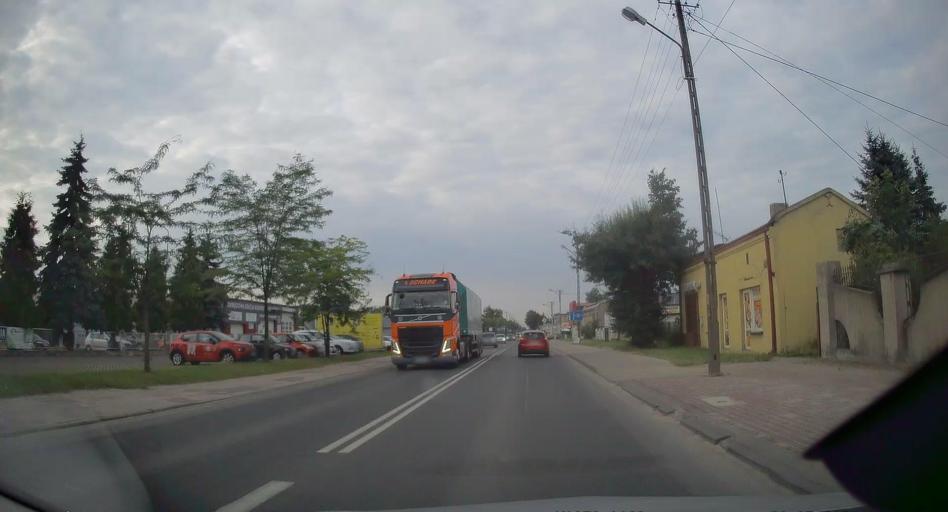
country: PL
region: Lodz Voivodeship
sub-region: Powiat radomszczanski
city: Radomsko
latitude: 51.0816
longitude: 19.4516
